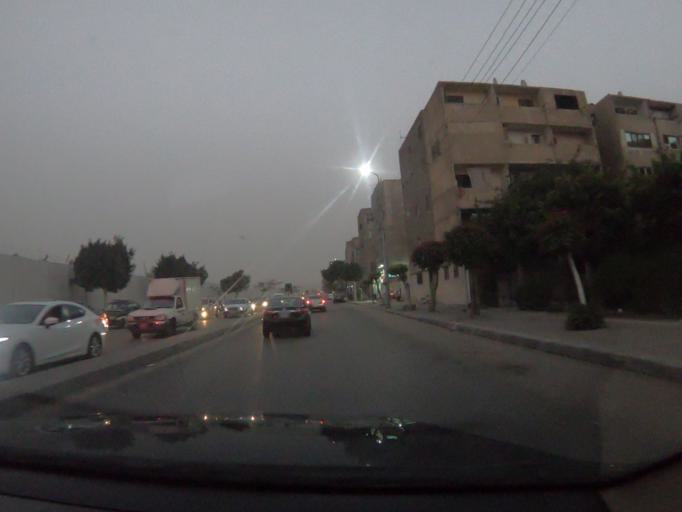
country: EG
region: Muhafazat al Qahirah
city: Cairo
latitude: 30.0841
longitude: 31.3551
